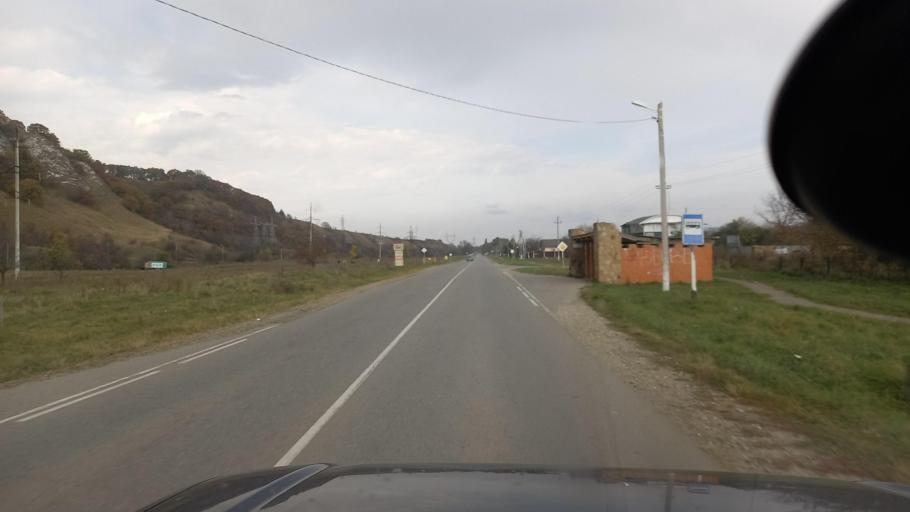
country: RU
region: Krasnodarskiy
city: Psebay
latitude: 44.1539
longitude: 40.8324
